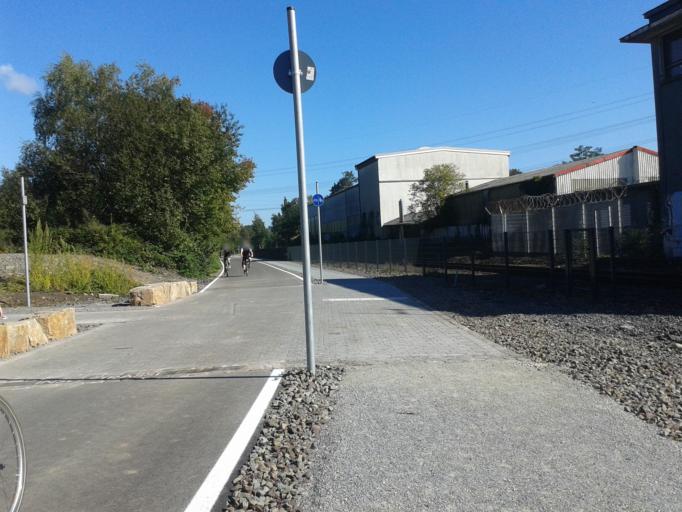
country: DE
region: North Rhine-Westphalia
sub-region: Regierungsbezirk Dusseldorf
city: Muelheim (Ruhr)
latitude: 51.4455
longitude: 6.9431
